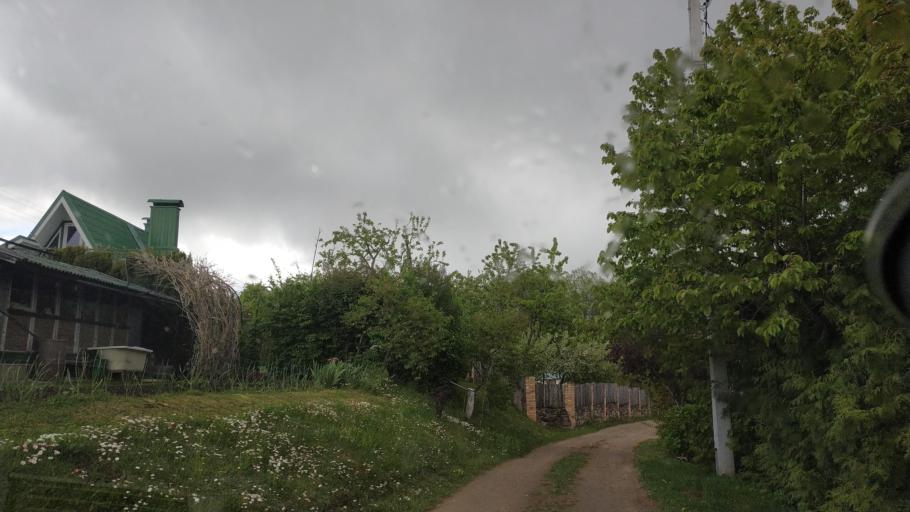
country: LT
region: Telsiu apskritis
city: Mazeikiai
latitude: 56.2863
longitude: 22.3471
